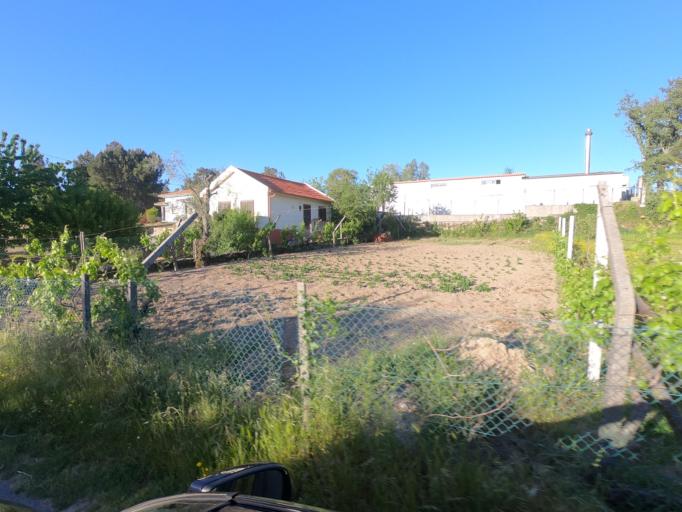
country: PT
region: Vila Real
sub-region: Vila Real
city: Vila Real
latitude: 41.3465
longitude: -7.7261
